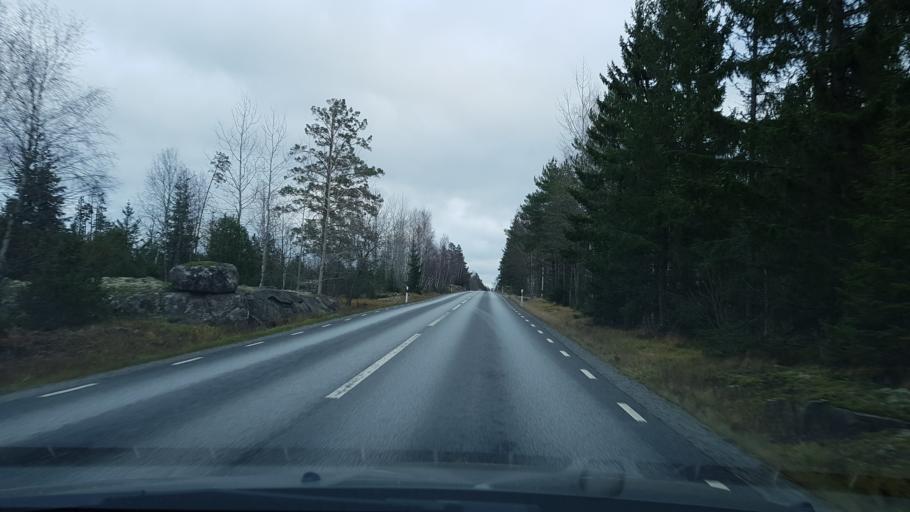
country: SE
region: Stockholm
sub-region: Norrtalje Kommun
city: Skanninge
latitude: 60.0348
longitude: 18.4760
